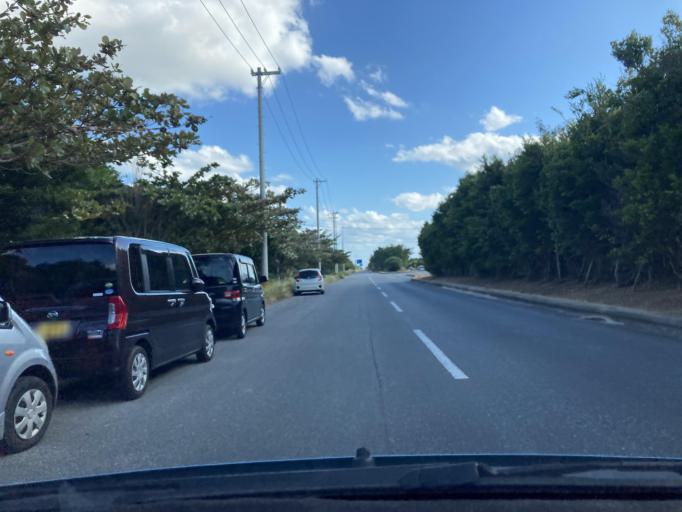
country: JP
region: Okinawa
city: Katsuren-haebaru
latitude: 26.3403
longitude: 127.8592
